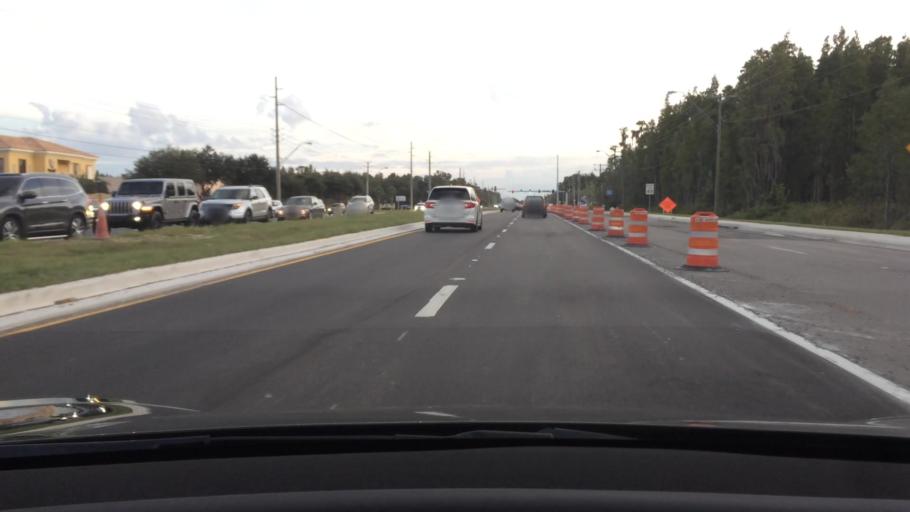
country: US
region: Florida
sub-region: Hillsborough County
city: Pebble Creek
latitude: 28.1710
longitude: -82.3538
